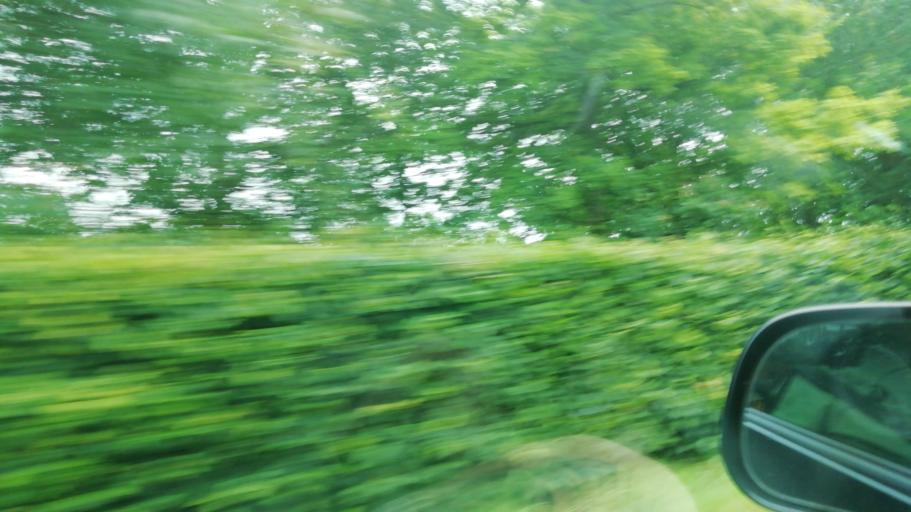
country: IE
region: Munster
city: Fethard
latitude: 52.4968
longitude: -7.6885
